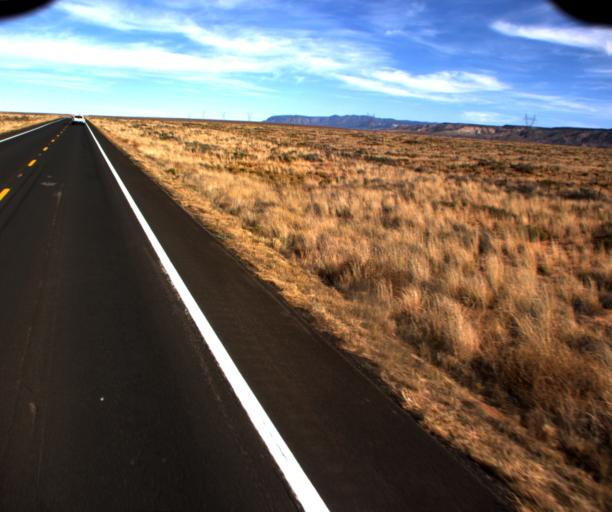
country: US
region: Arizona
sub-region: Apache County
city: Lukachukai
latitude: 36.9639
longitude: -109.4752
